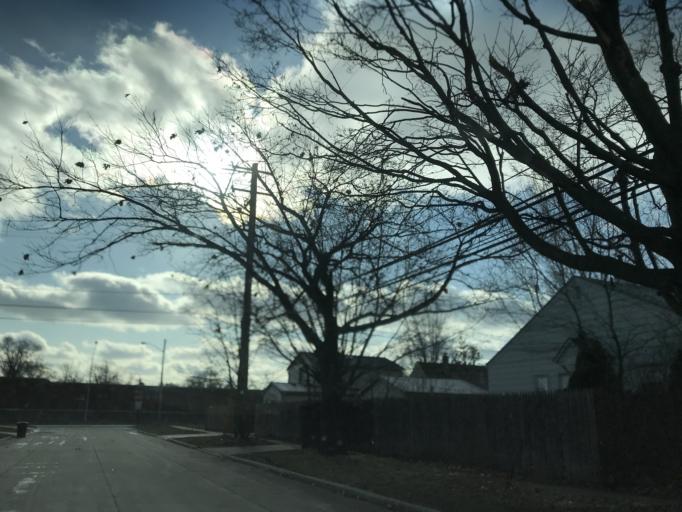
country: US
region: Michigan
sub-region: Oakland County
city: Madison Heights
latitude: 42.4774
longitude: -83.1171
